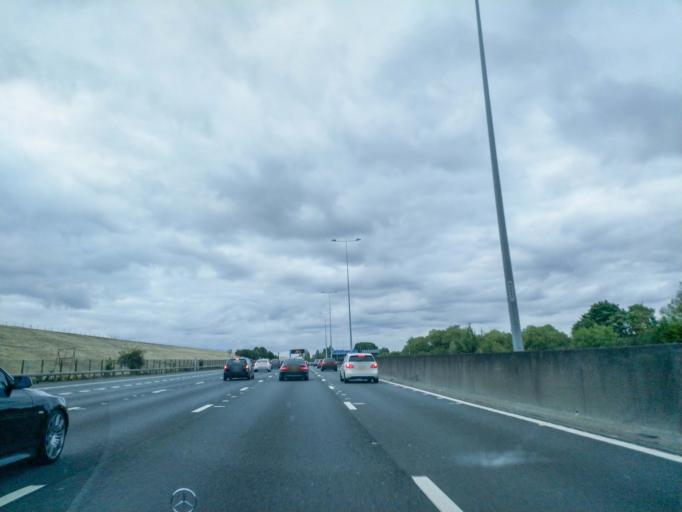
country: GB
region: England
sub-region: Surrey
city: Colnbrook
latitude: 51.4558
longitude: -0.5193
